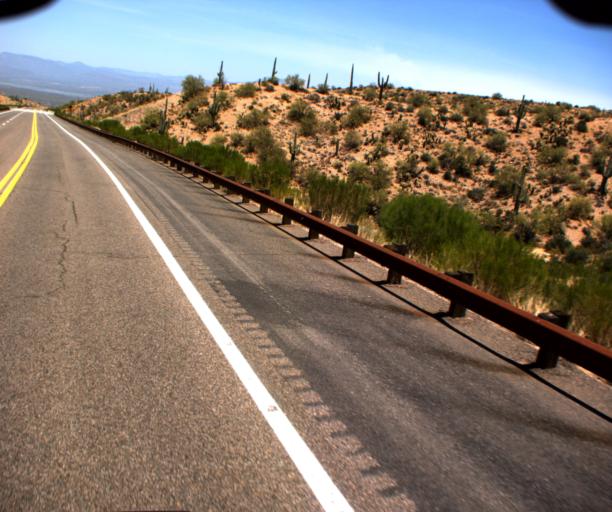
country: US
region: Arizona
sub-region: Gila County
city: Miami
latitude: 33.5585
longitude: -110.9497
